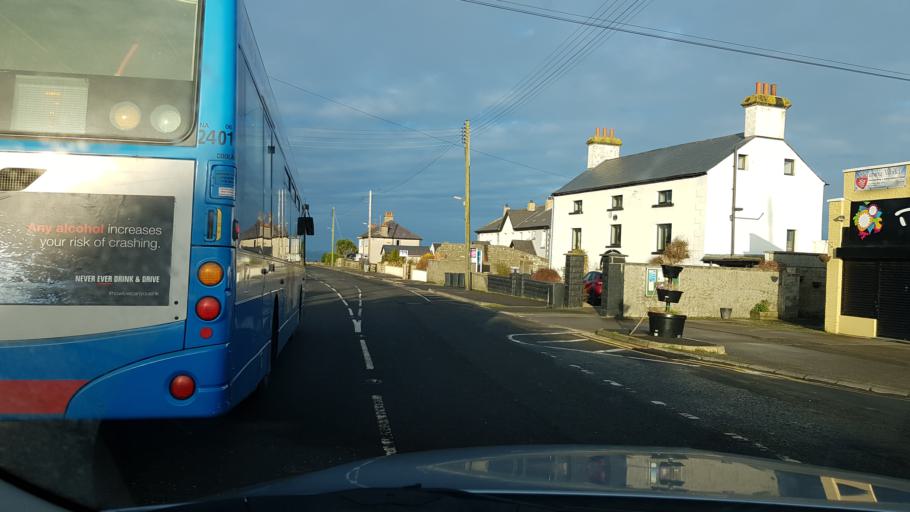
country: GB
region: Northern Ireland
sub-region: Down District
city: Millisle
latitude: 54.6090
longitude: -5.5289
